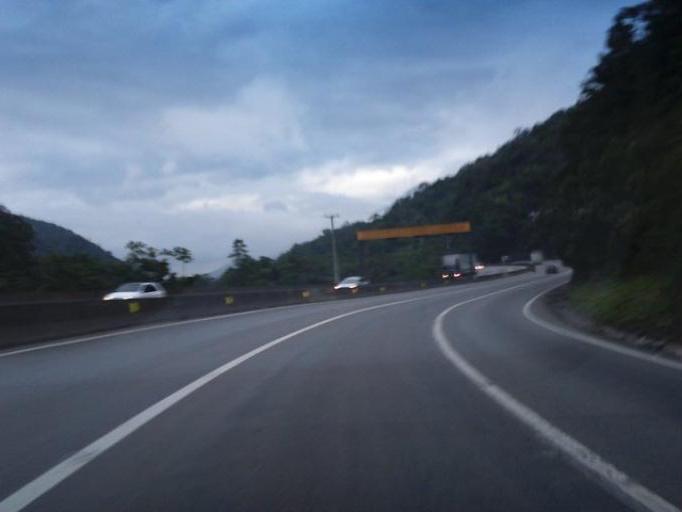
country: BR
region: Parana
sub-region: Guaratuba
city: Guaratuba
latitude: -25.8735
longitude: -48.9360
